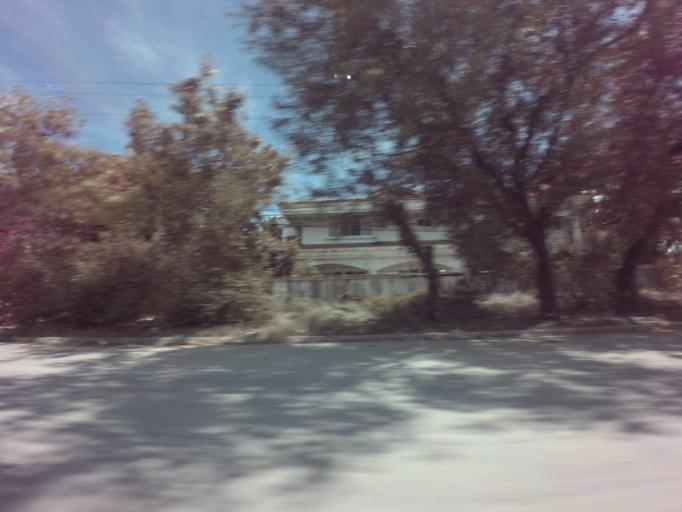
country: PH
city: Sambayanihan People's Village
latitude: 14.5078
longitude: 120.9833
